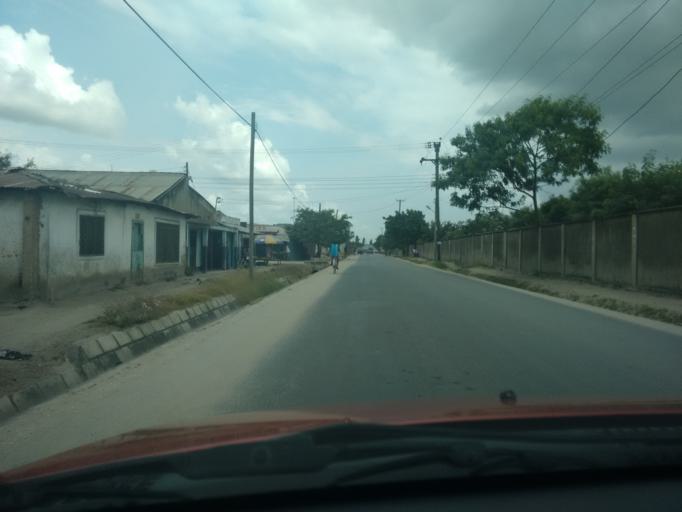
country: TZ
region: Dar es Salaam
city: Dar es Salaam
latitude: -6.8546
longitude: 39.2498
